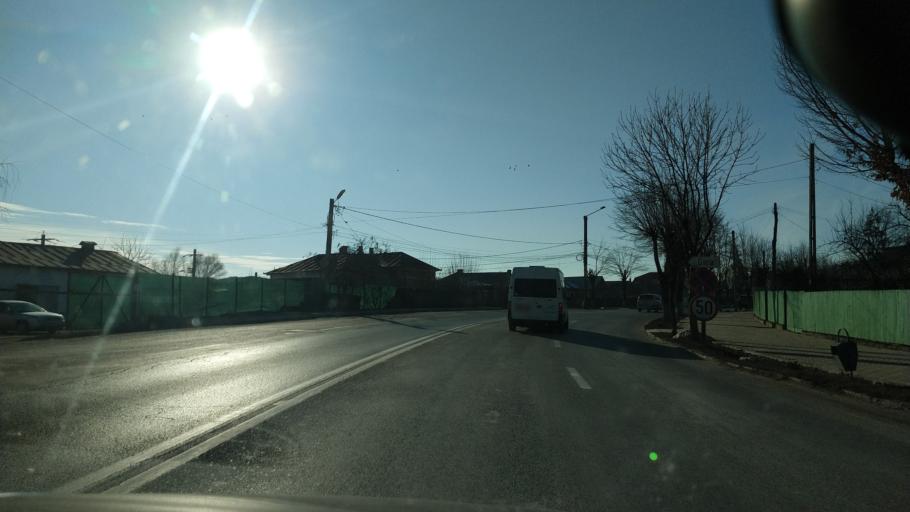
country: RO
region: Iasi
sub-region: Comuna Ion Neculce
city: Buznea
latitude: 47.2116
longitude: 27.0241
